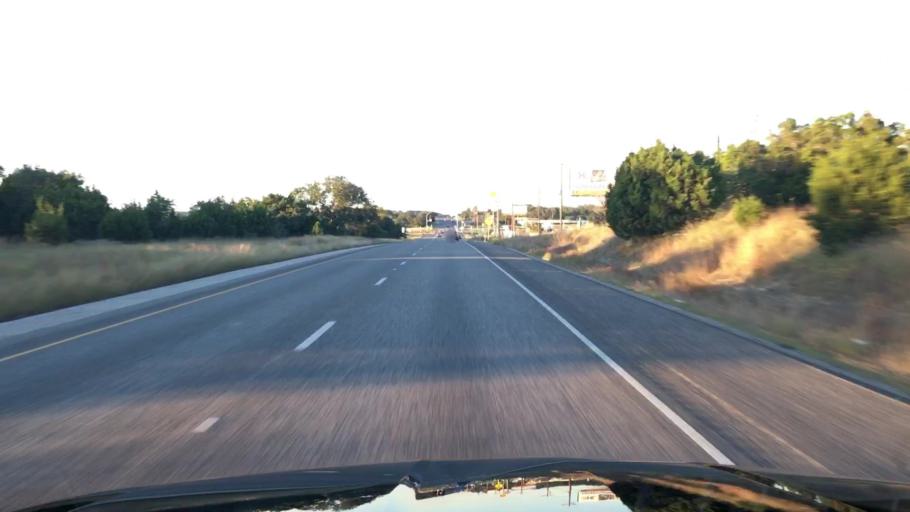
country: US
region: Texas
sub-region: Comal County
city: Canyon Lake
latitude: 29.9337
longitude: -98.4105
